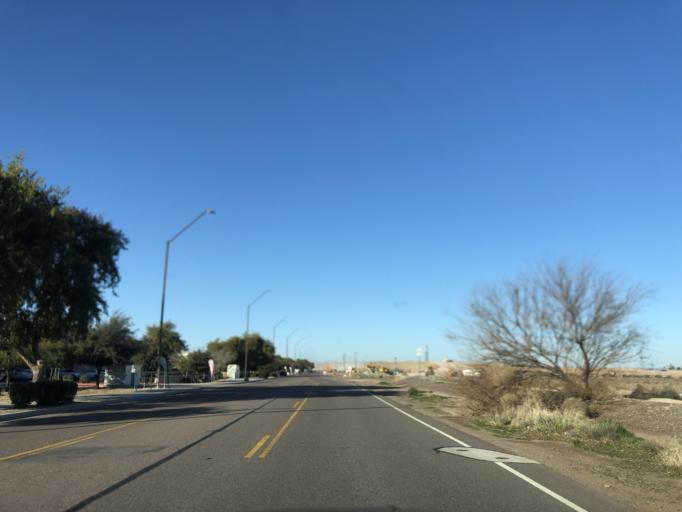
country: US
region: Arizona
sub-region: Maricopa County
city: Avondale
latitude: 33.4523
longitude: -112.3238
